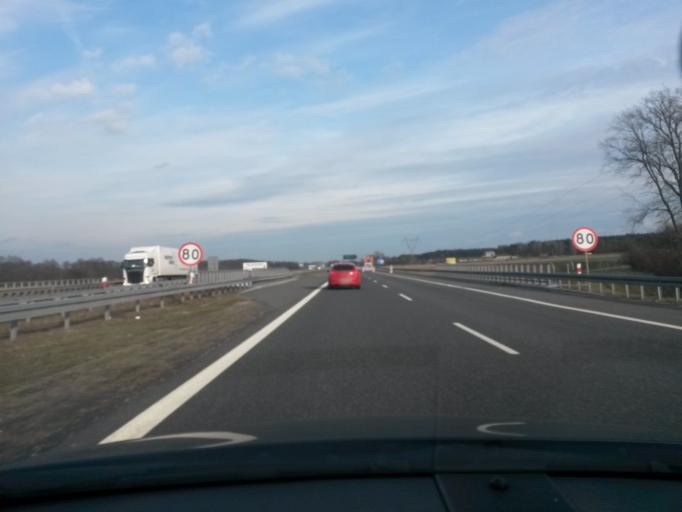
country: PL
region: Lodz Voivodeship
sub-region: Powiat zgierski
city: Ozorkow
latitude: 51.9257
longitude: 19.3283
